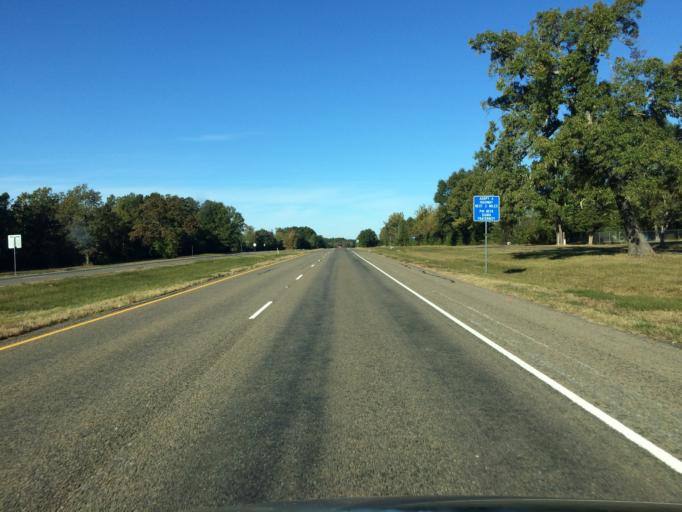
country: US
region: Texas
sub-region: Wood County
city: Hawkins
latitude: 32.5958
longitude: -95.2447
